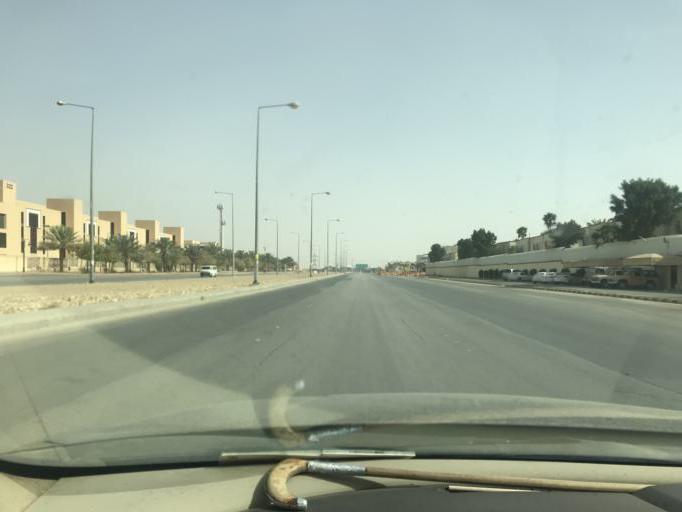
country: SA
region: Ar Riyad
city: Riyadh
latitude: 24.8112
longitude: 46.6910
